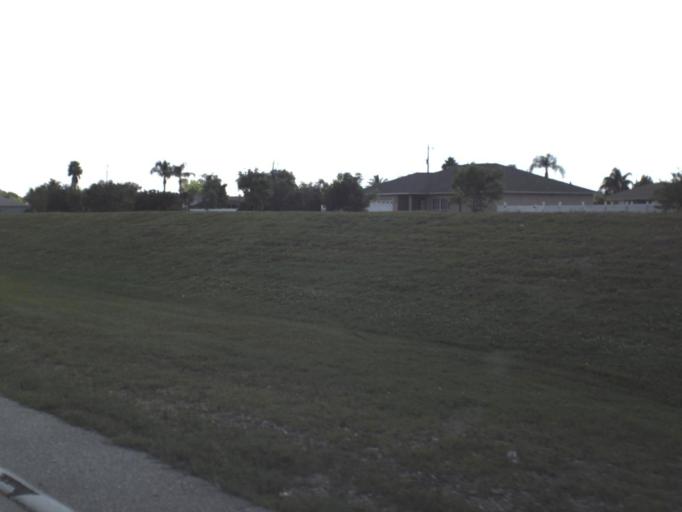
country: US
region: Florida
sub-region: Lee County
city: Cape Coral
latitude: 26.6042
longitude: -81.9636
